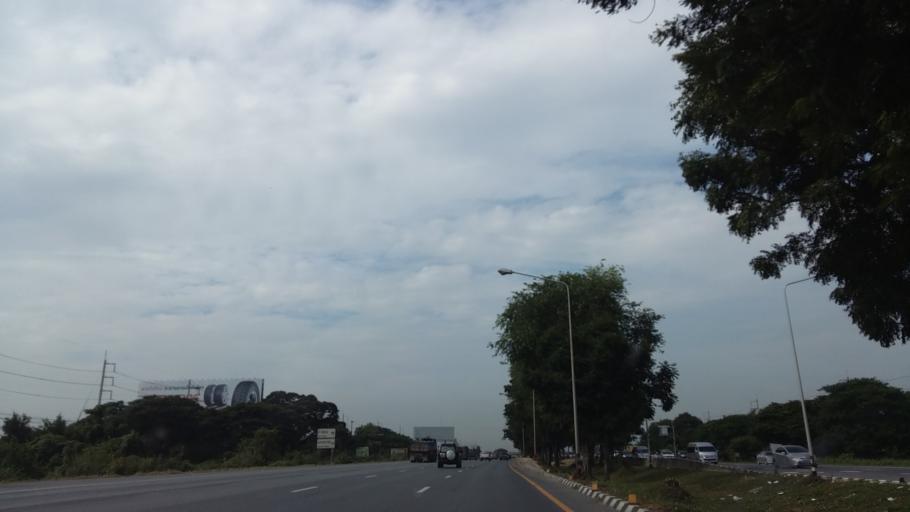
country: TH
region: Phra Nakhon Si Ayutthaya
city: Bang Pahan
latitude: 14.4939
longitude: 100.5241
